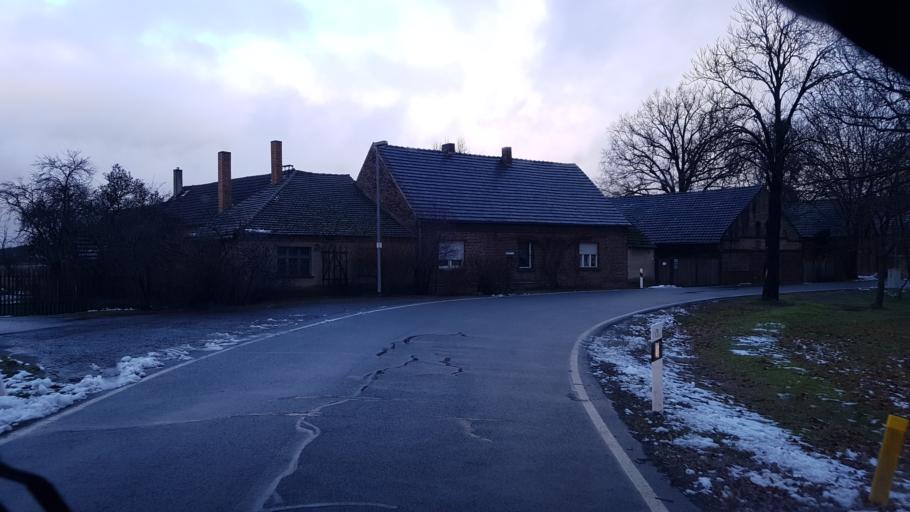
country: DE
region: Brandenburg
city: Heinersbruck
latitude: 51.8335
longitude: 14.5048
